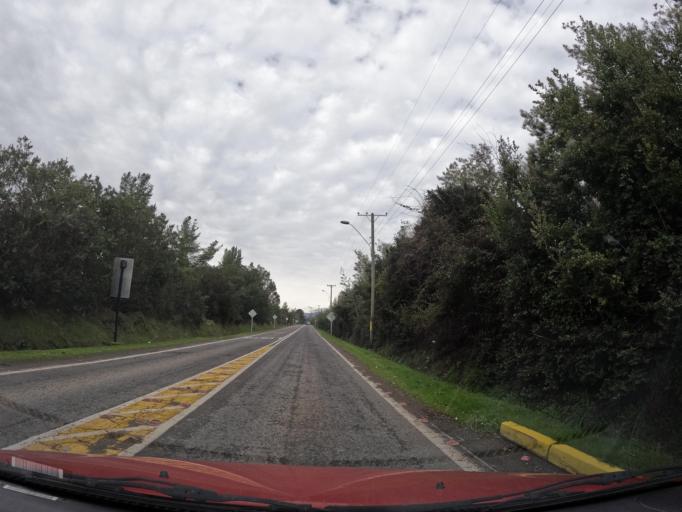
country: CL
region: Maule
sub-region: Provincia de Linares
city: Linares
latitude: -35.8957
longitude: -71.5207
